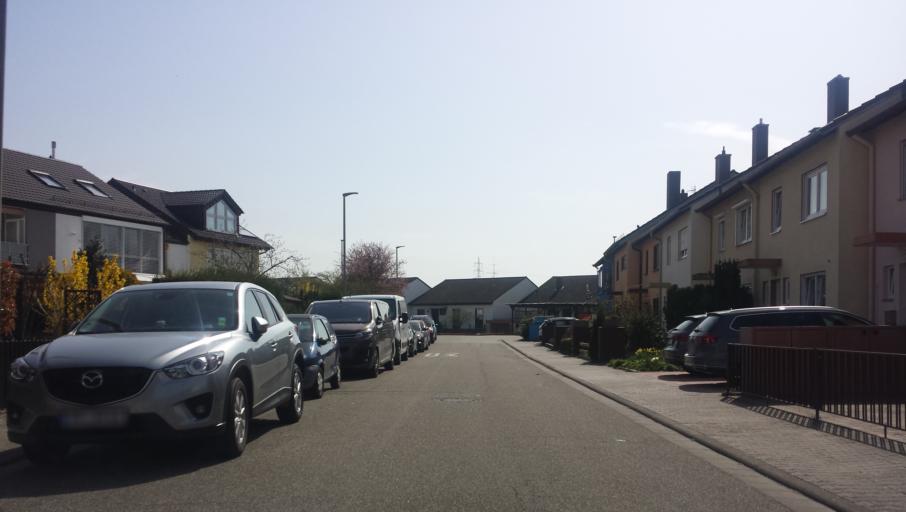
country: DE
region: Rheinland-Pfalz
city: Mutterstadt
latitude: 49.4348
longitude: 8.3631
